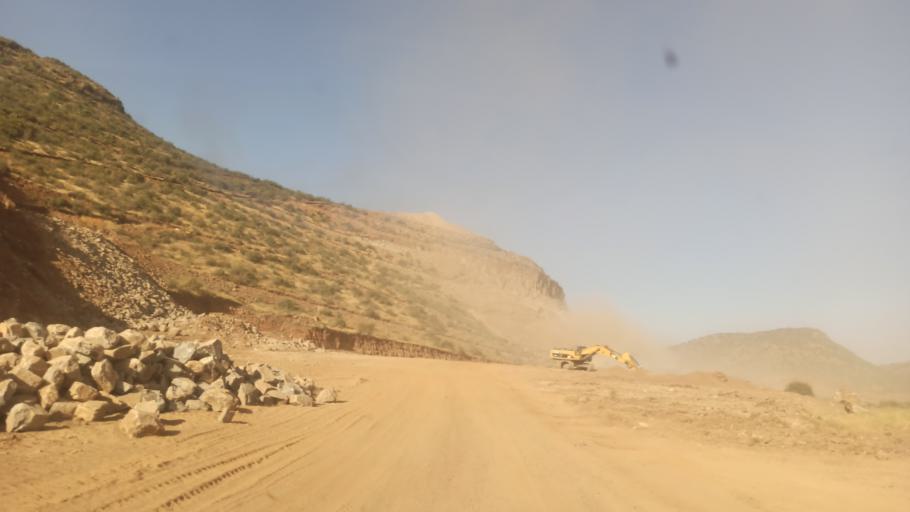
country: ET
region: Oromiya
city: Ziway
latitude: 7.9375
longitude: 38.6155
